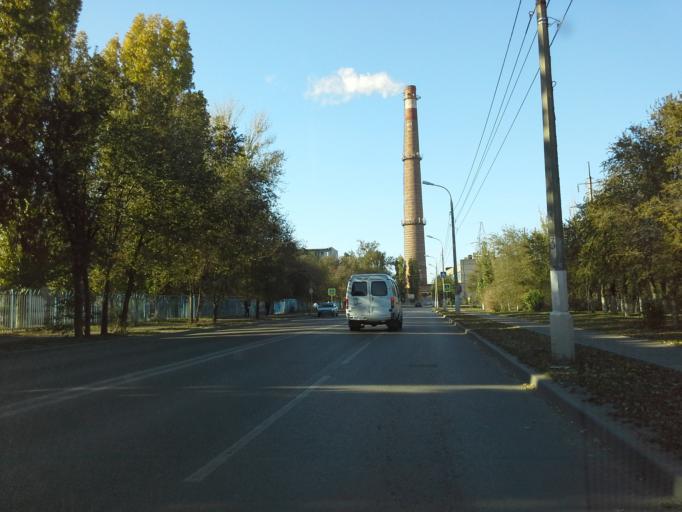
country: RU
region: Volgograd
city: Vodstroy
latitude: 48.8236
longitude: 44.6294
